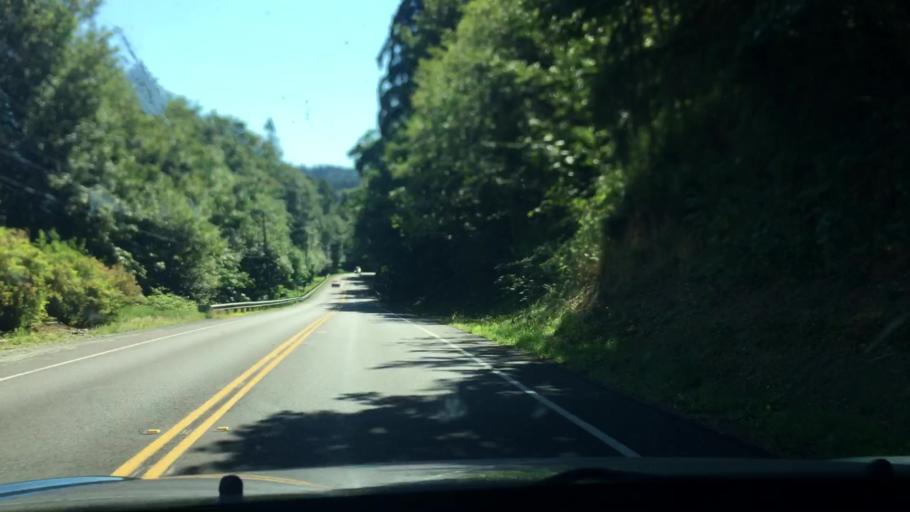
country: US
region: Washington
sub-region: King County
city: Newcastle
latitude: 47.5389
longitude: -122.1410
